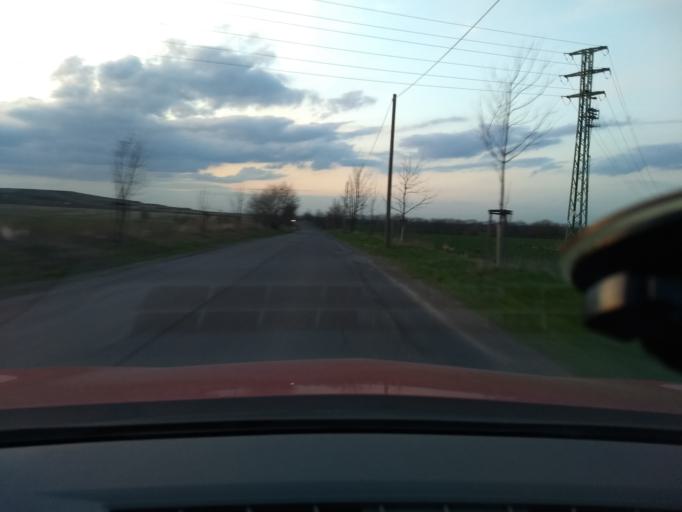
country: CZ
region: Central Bohemia
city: Rudna
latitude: 50.0520
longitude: 14.2539
